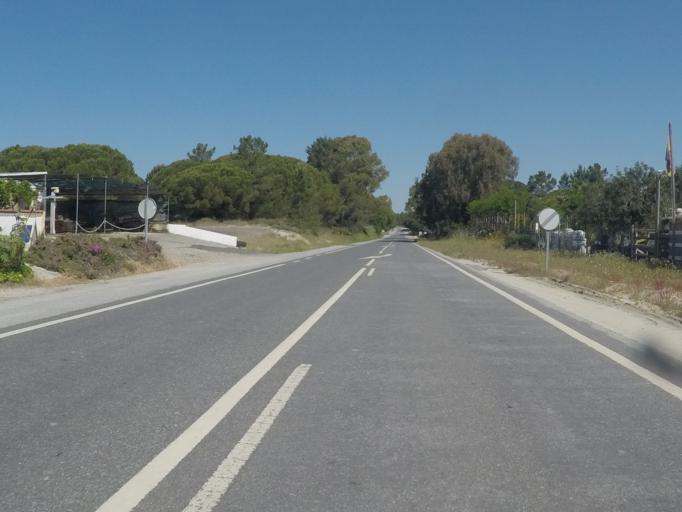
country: PT
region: Setubal
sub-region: Grandola
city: Grandola
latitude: 38.3103
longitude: -8.7429
